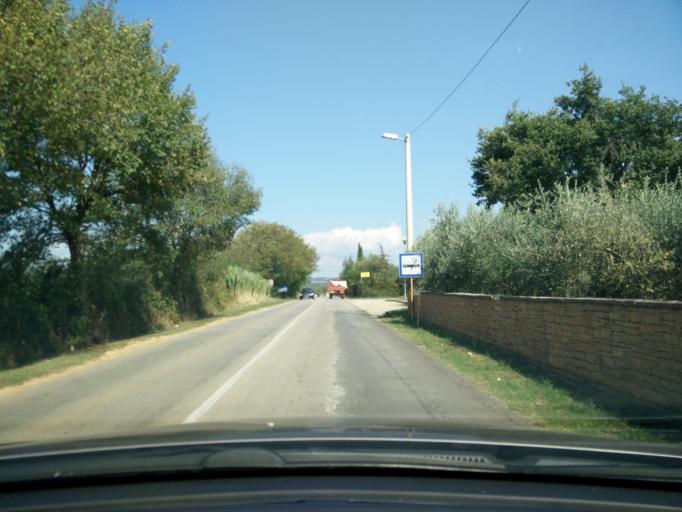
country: HR
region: Istarska
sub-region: Grad Porec
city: Porec
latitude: 45.2662
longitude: 13.6389
